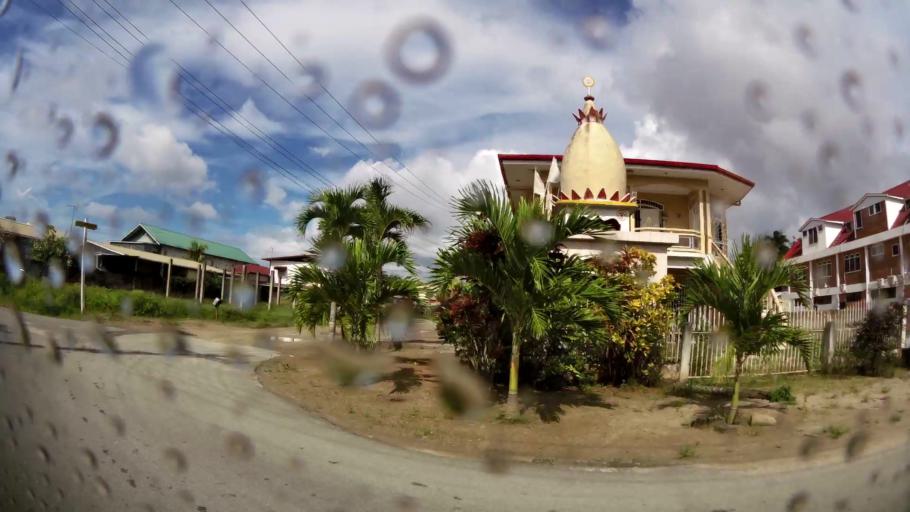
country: SR
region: Paramaribo
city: Paramaribo
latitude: 5.8436
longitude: -55.2065
